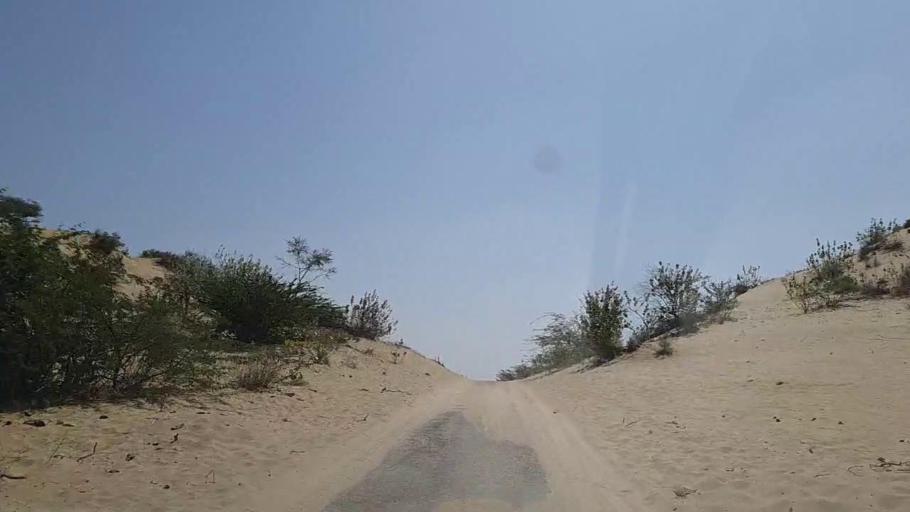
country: PK
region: Sindh
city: Diplo
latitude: 24.5096
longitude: 69.4223
